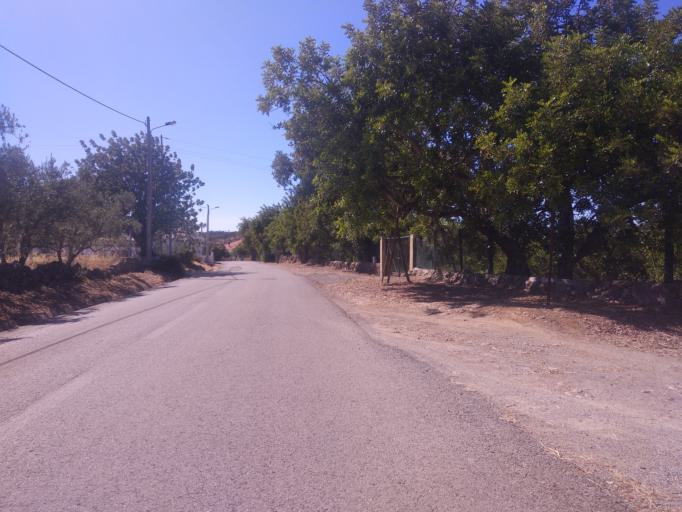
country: PT
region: Faro
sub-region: Sao Bras de Alportel
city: Sao Bras de Alportel
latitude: 37.1700
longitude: -7.8862
